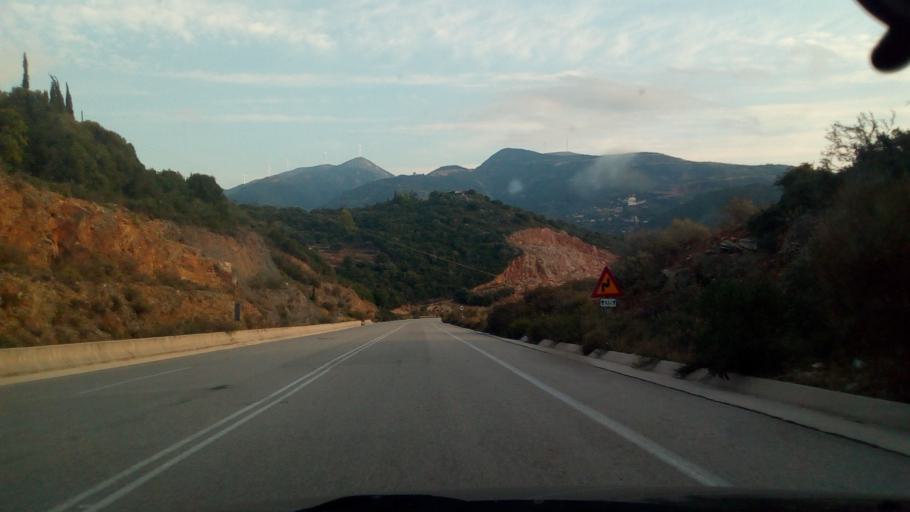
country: GR
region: West Greece
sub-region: Nomos Aitolias kai Akarnanias
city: Nafpaktos
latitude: 38.4033
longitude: 21.8363
